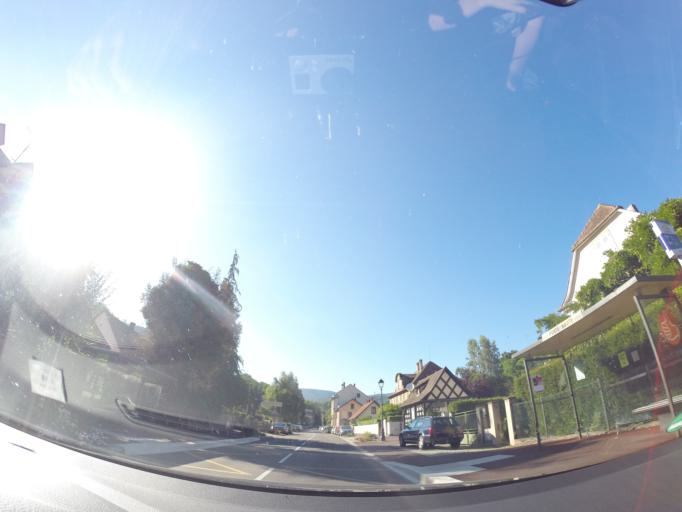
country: FR
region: Alsace
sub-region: Departement du Haut-Rhin
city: Kaysersberg
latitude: 48.1412
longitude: 7.2586
